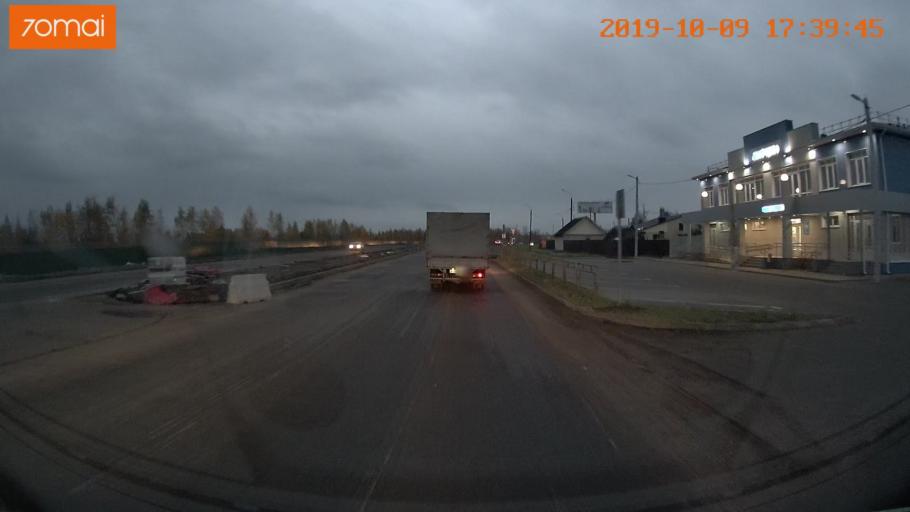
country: RU
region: Ivanovo
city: Bogorodskoye
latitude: 57.0581
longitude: 40.9611
